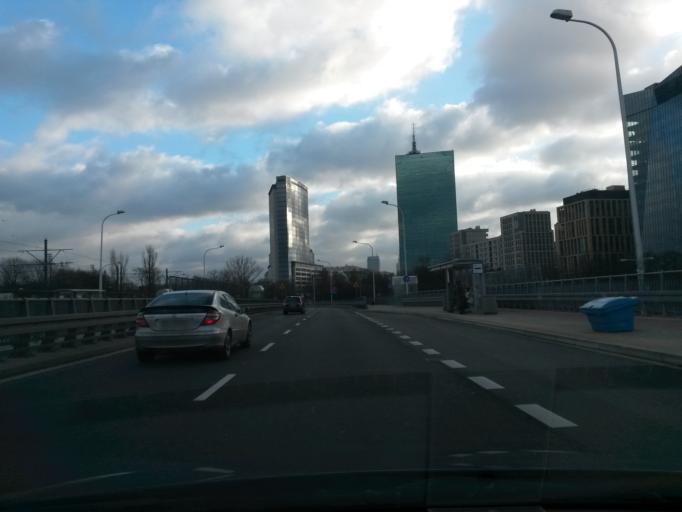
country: PL
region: Masovian Voivodeship
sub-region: Warszawa
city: Zoliborz
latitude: 52.2585
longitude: 20.9956
